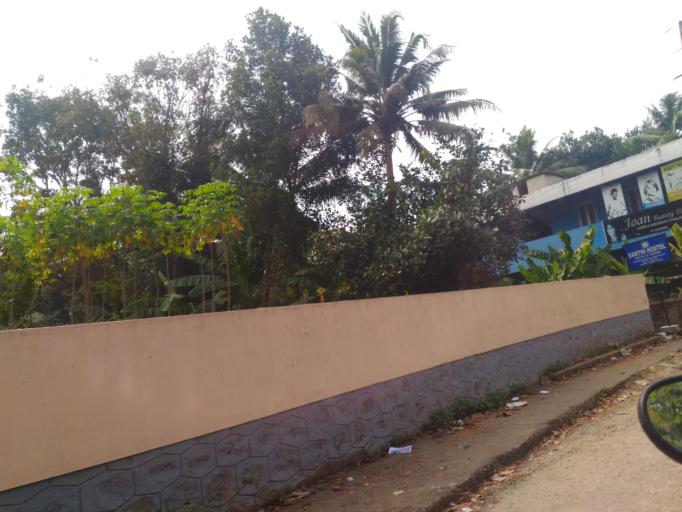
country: IN
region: Kerala
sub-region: Kottayam
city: Lalam
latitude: 9.7099
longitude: 76.6722
